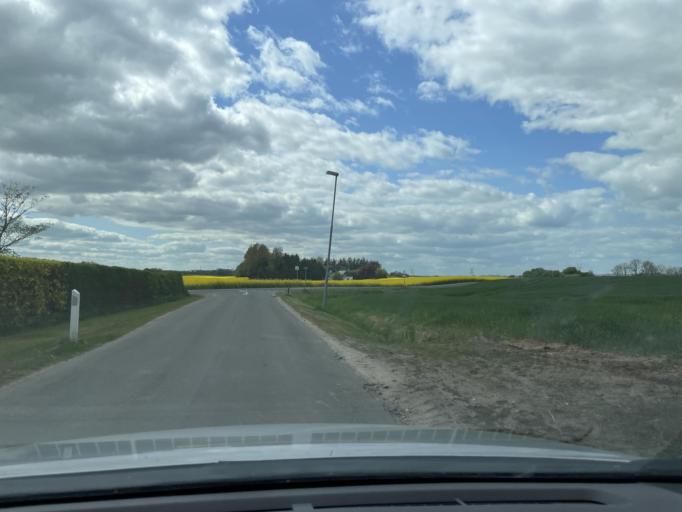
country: DK
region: Central Jutland
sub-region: Skanderborg Kommune
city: Skanderborg
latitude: 55.9203
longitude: 9.9668
